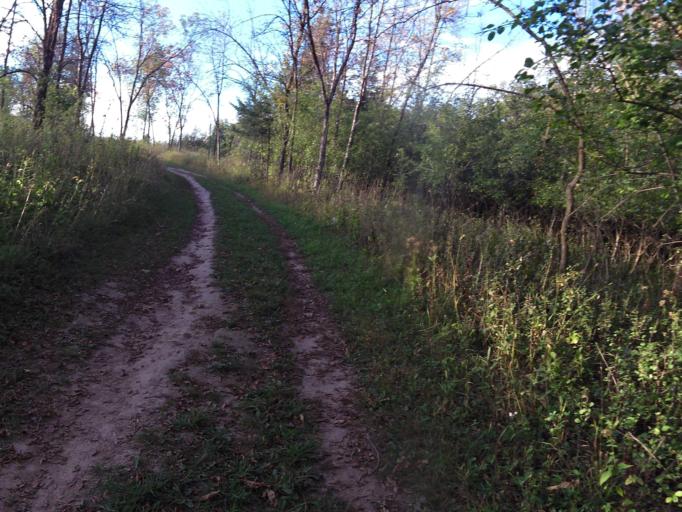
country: US
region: Minnesota
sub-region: Washington County
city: Afton
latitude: 44.8660
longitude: -92.7846
